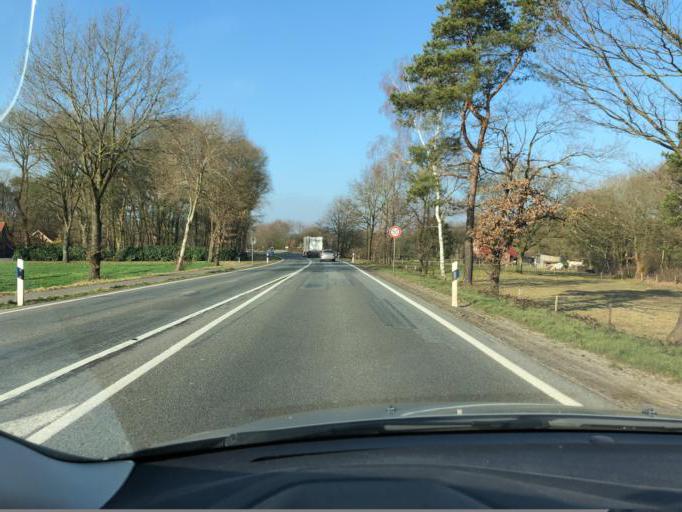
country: DE
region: Lower Saxony
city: Schwerinsdorf
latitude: 53.3063
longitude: 7.7695
